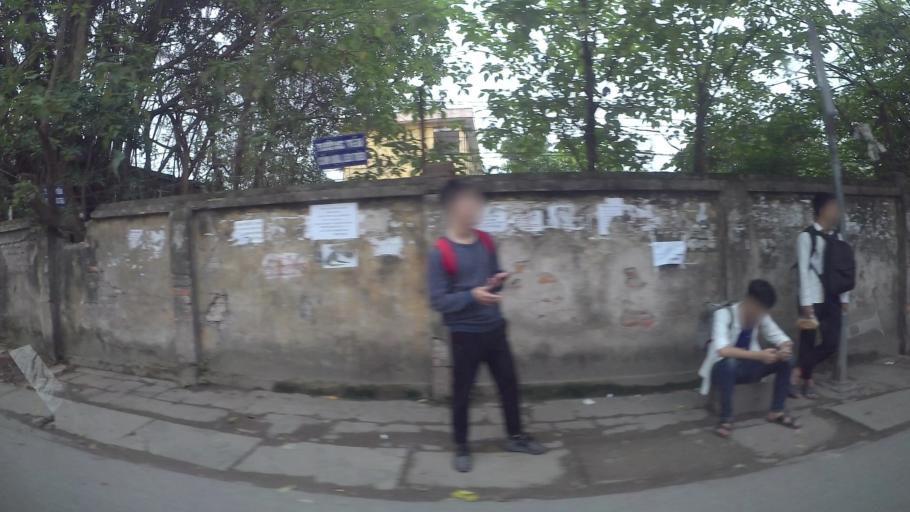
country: VN
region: Ha Noi
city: Hai BaTrung
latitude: 20.9828
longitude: 105.8773
